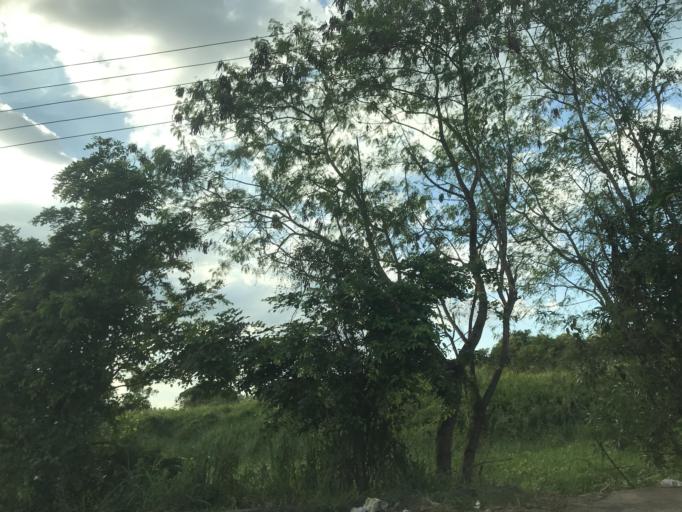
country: LK
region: Western
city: Gampaha
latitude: 7.0835
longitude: 79.9869
